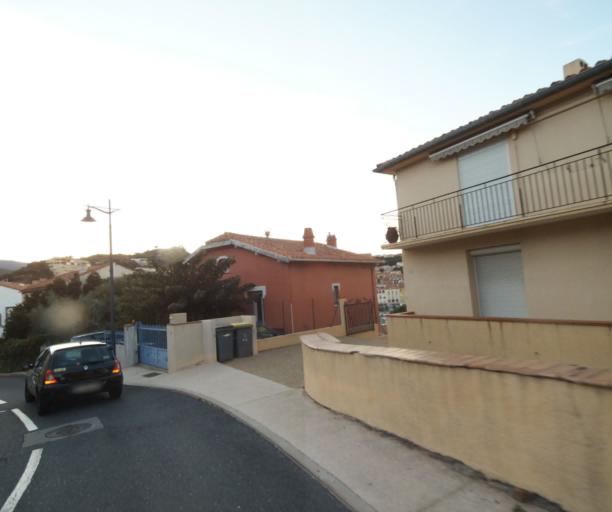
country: FR
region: Languedoc-Roussillon
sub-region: Departement des Pyrenees-Orientales
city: Portvendres
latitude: 42.5157
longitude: 3.1085
